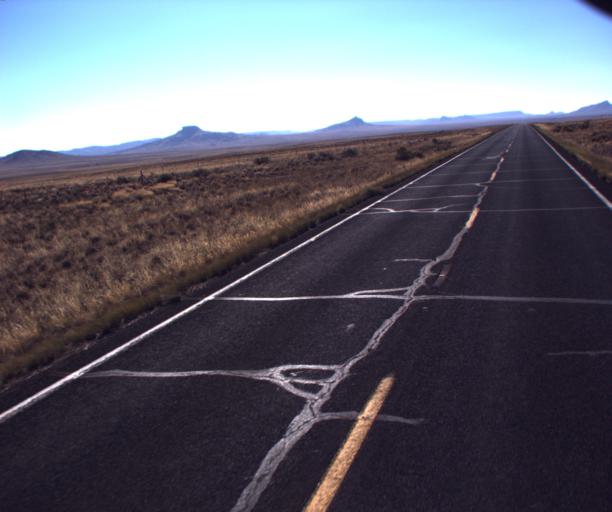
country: US
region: Arizona
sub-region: Navajo County
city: First Mesa
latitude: 35.6358
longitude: -110.4839
